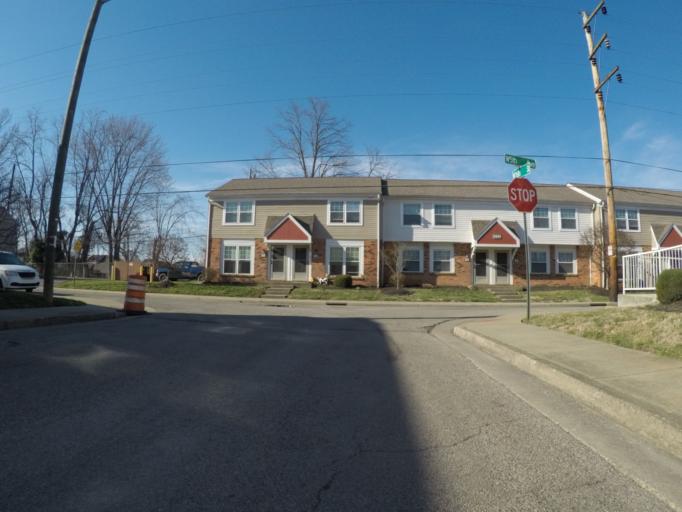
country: US
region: Ohio
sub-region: Lawrence County
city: Burlington
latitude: 38.4067
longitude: -82.4949
